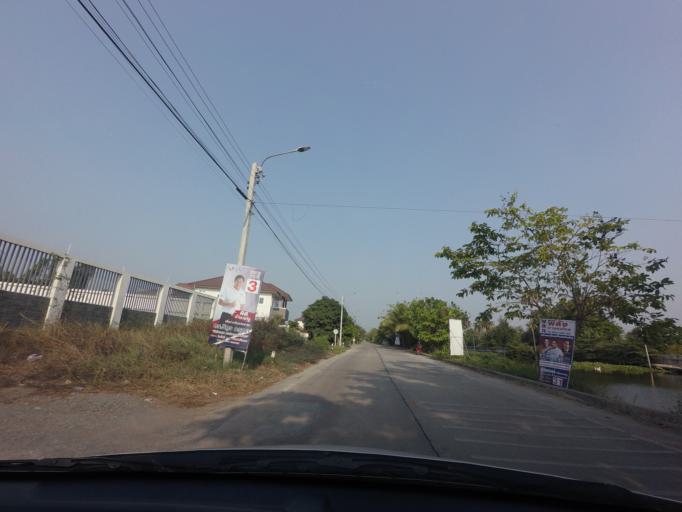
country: TH
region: Nonthaburi
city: Bang Yai
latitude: 13.8028
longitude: 100.3776
